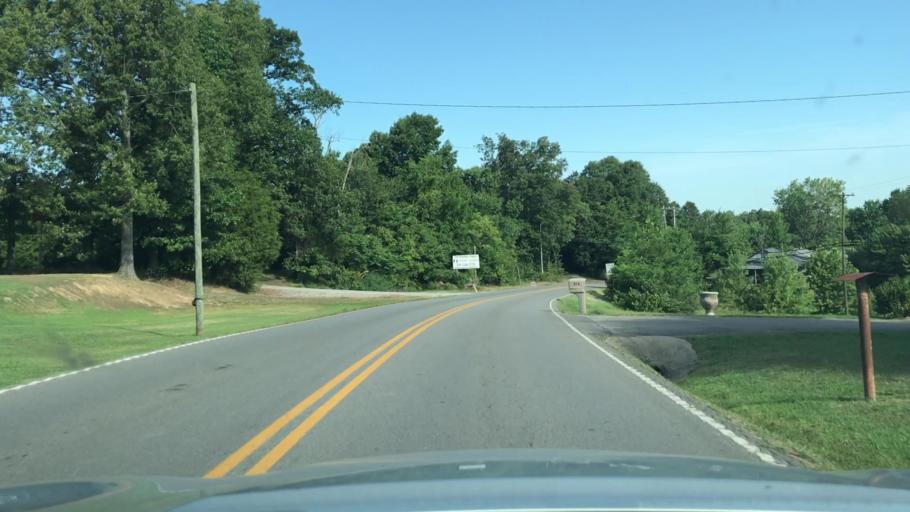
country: US
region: Kentucky
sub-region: Muhlenberg County
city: Greenville
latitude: 37.1897
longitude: -87.1708
